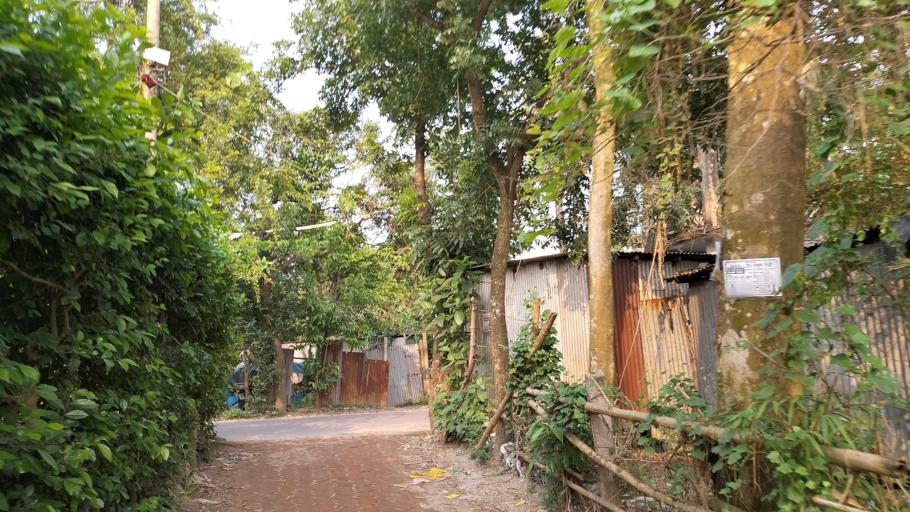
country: BD
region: Dhaka
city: Azimpur
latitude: 23.6692
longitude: 90.3220
